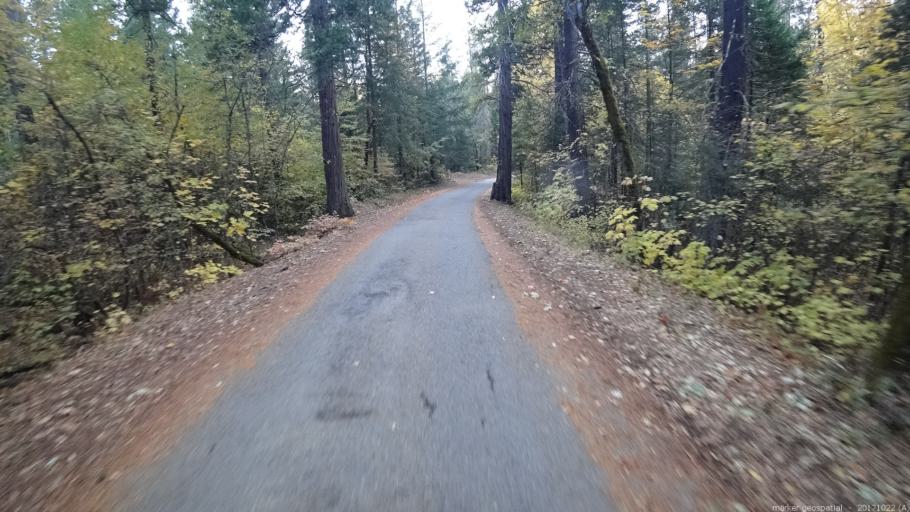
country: US
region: California
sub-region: Siskiyou County
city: Dunsmuir
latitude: 41.1694
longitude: -122.2700
